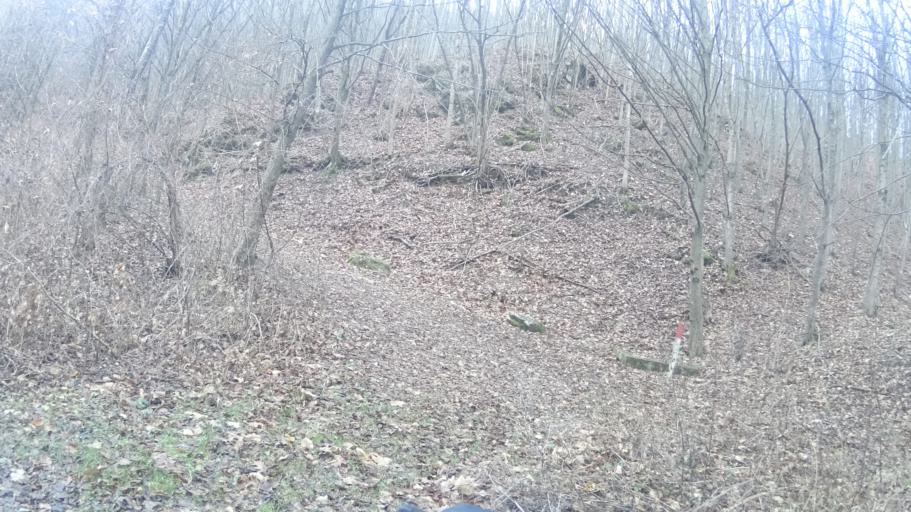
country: HU
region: Borsod-Abauj-Zemplen
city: Bogacs
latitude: 47.9802
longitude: 20.5190
